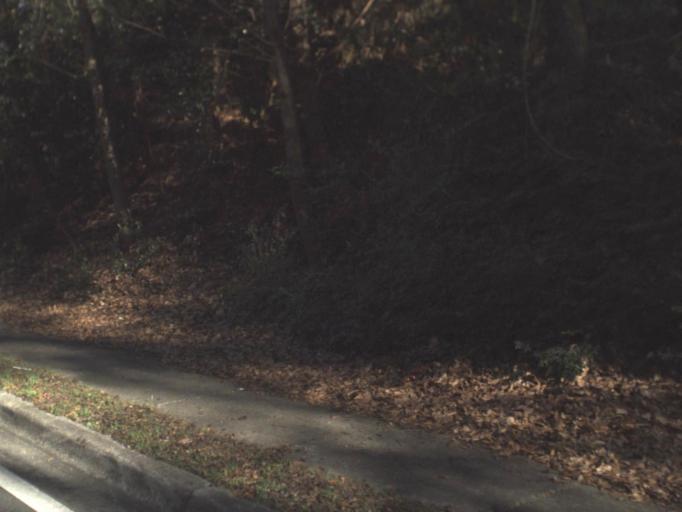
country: US
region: Florida
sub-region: Leon County
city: Tallahassee
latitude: 30.4458
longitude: -84.2672
